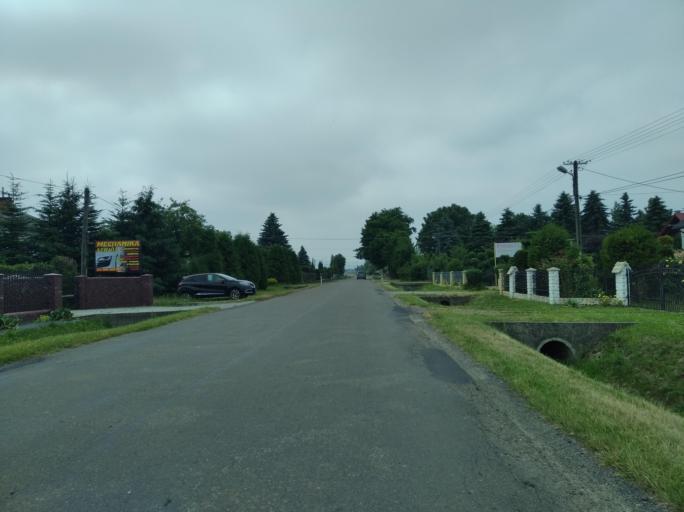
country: PL
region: Subcarpathian Voivodeship
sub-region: Powiat krosnienski
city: Sieniawa
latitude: 49.5704
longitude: 21.9233
